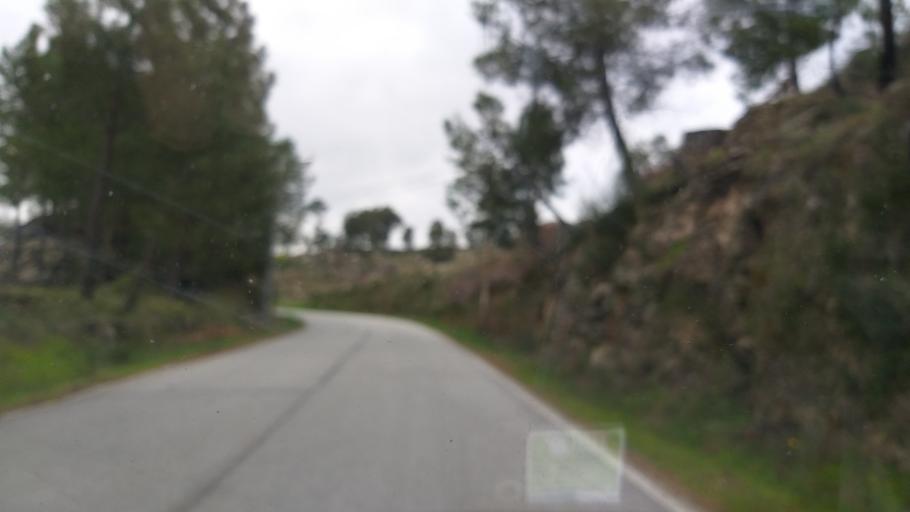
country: PT
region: Guarda
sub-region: Fornos de Algodres
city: Fornos de Algodres
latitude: 40.5741
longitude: -7.6055
